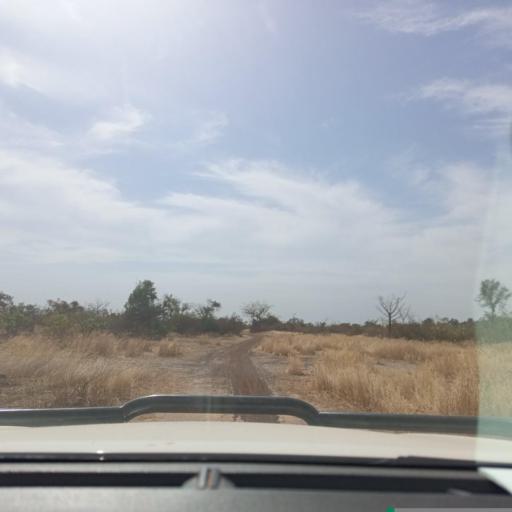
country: ML
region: Koulikoro
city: Kati
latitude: 12.7351
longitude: -8.2527
